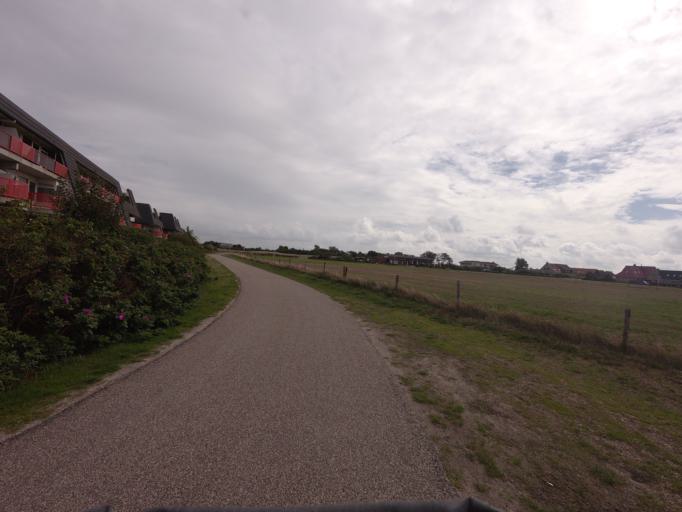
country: NL
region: Friesland
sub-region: Gemeente Ameland
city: Nes
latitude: 53.4527
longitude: 5.8000
